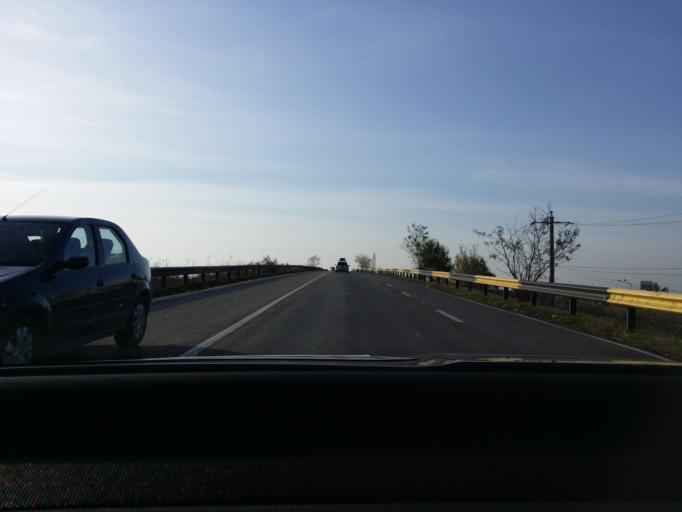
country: RO
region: Prahova
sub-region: Comuna Targsoru Vechi
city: Strejnicu
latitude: 44.9400
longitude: 25.9704
